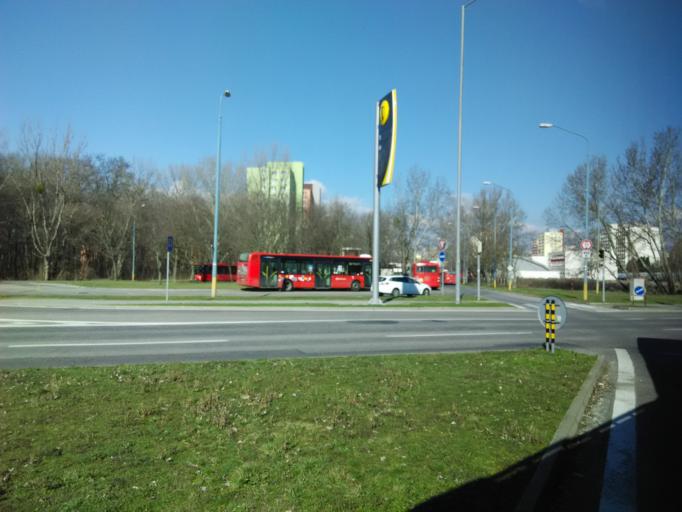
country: SK
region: Bratislavsky
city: Bratislava
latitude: 48.1168
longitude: 17.1334
